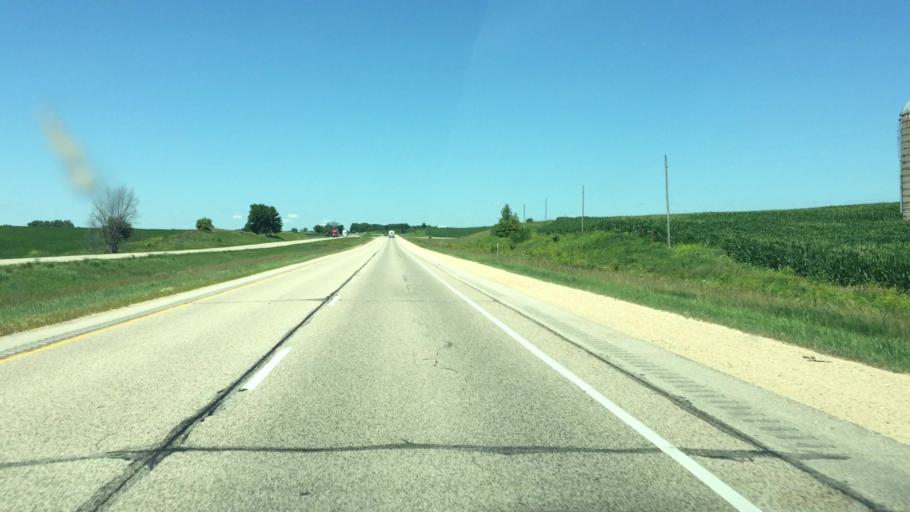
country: US
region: Iowa
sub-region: Jackson County
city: Maquoketa
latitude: 42.2022
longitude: -90.6700
